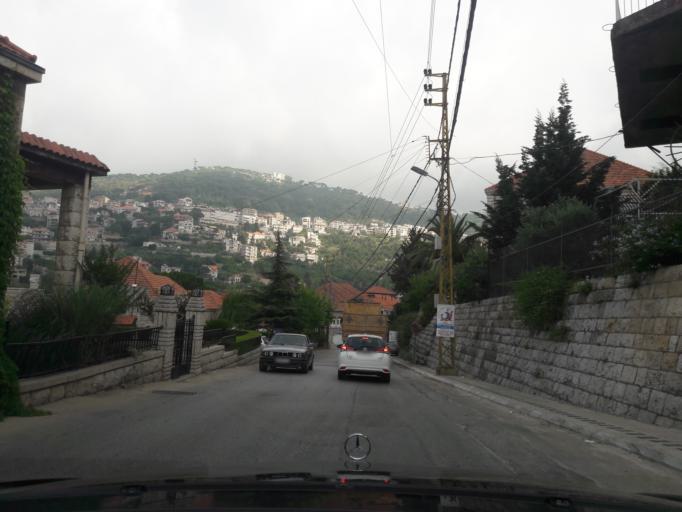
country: LB
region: Mont-Liban
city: Djounie
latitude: 33.9283
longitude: 35.7310
